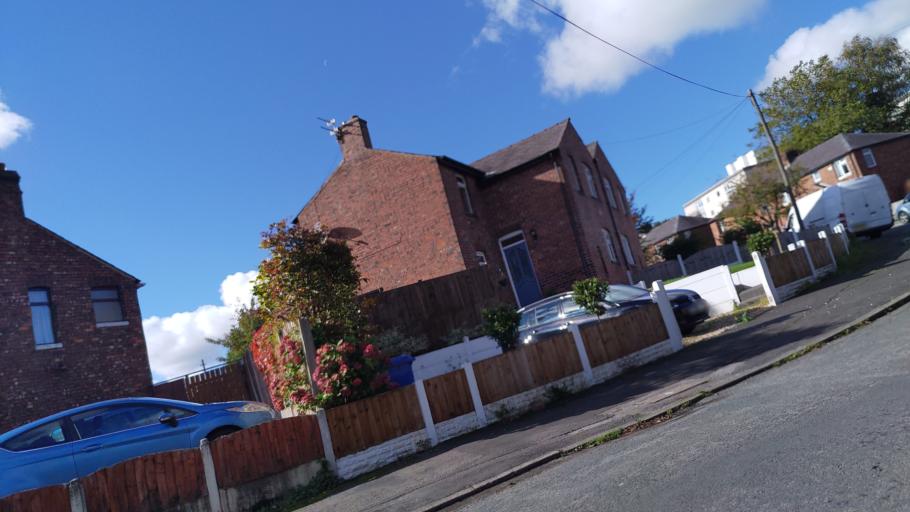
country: GB
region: England
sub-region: Lancashire
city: Chorley
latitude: 53.6635
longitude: -2.6294
